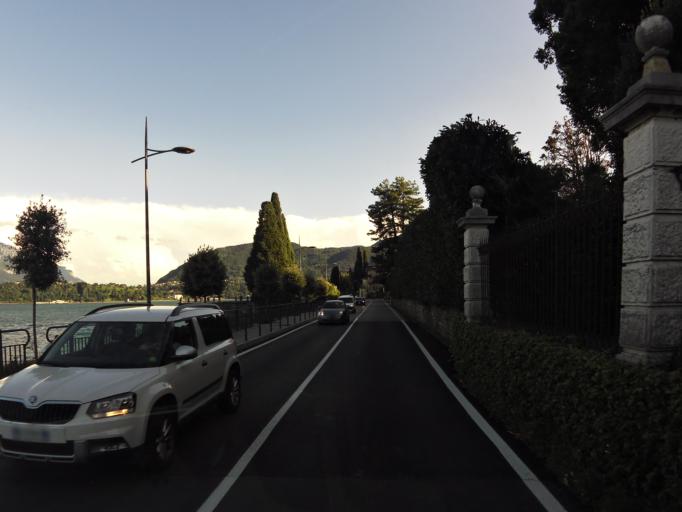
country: IT
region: Lombardy
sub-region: Provincia di Como
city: Griante
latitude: 45.9970
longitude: 9.2385
